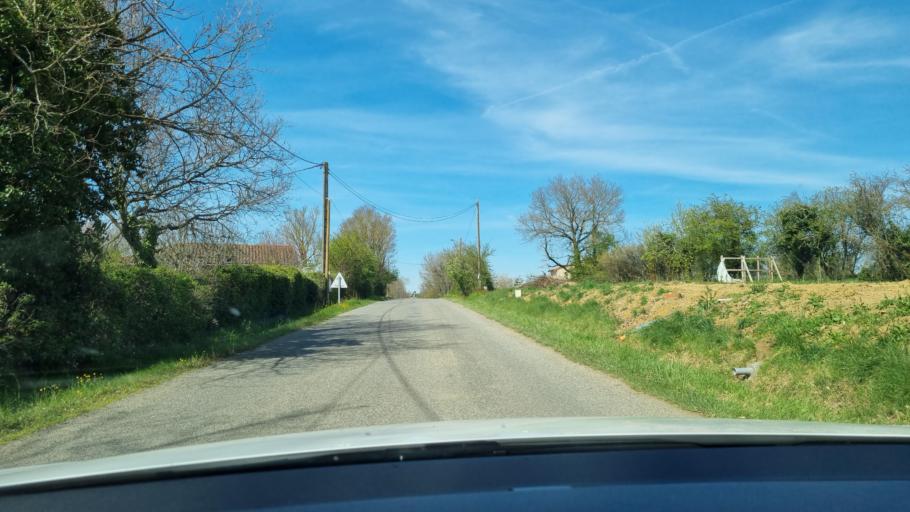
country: FR
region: Midi-Pyrenees
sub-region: Departement de la Haute-Garonne
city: Rieumes
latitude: 43.4683
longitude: 1.0627
